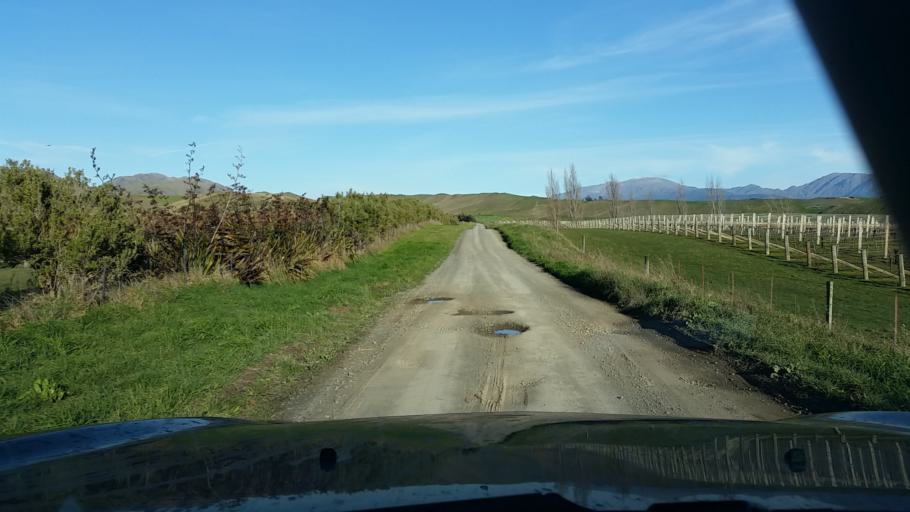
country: NZ
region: Marlborough
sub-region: Marlborough District
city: Blenheim
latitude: -41.7071
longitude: 174.0294
